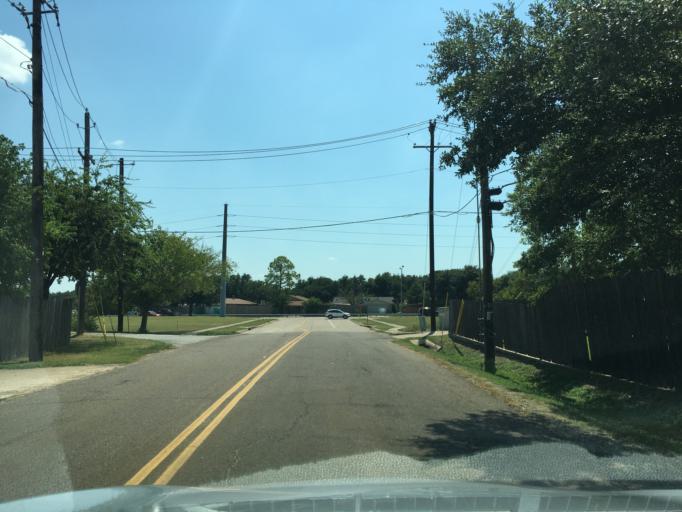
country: US
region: Texas
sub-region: Dallas County
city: Garland
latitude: 32.9617
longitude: -96.6699
